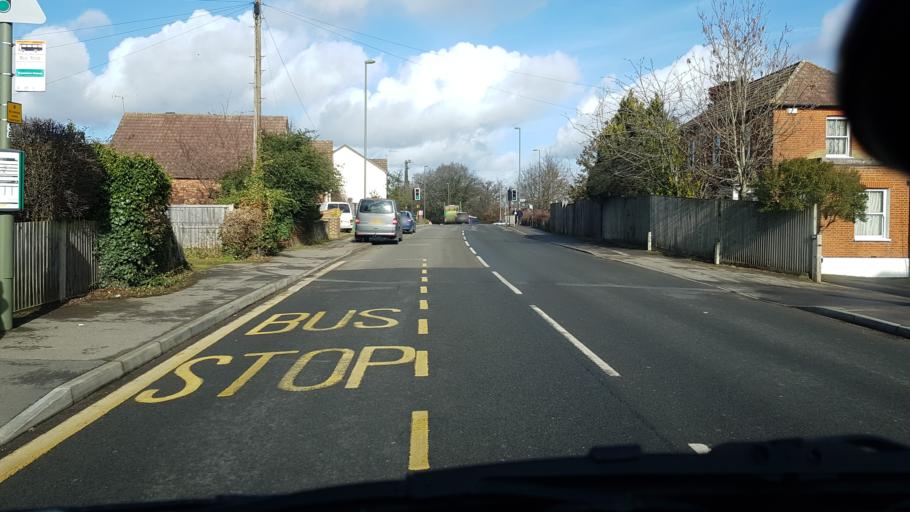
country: GB
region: England
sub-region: Surrey
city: Guildford
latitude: 51.2587
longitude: -0.5950
